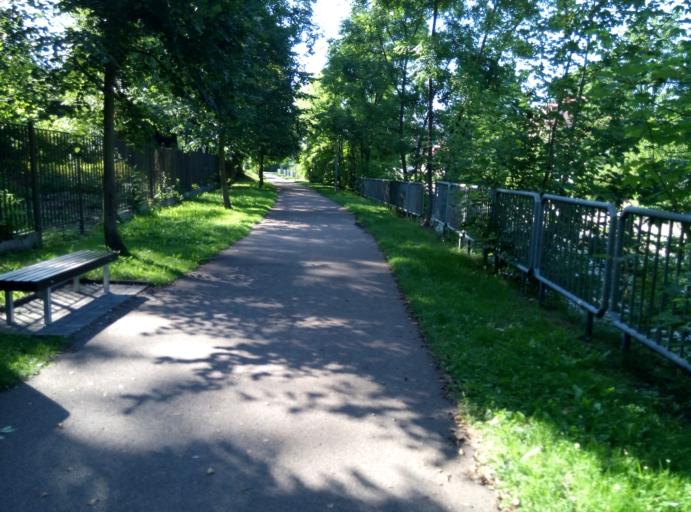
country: CZ
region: Plzensky
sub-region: Okres Rokycany
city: Rokycany
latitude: 49.7391
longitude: 13.6046
